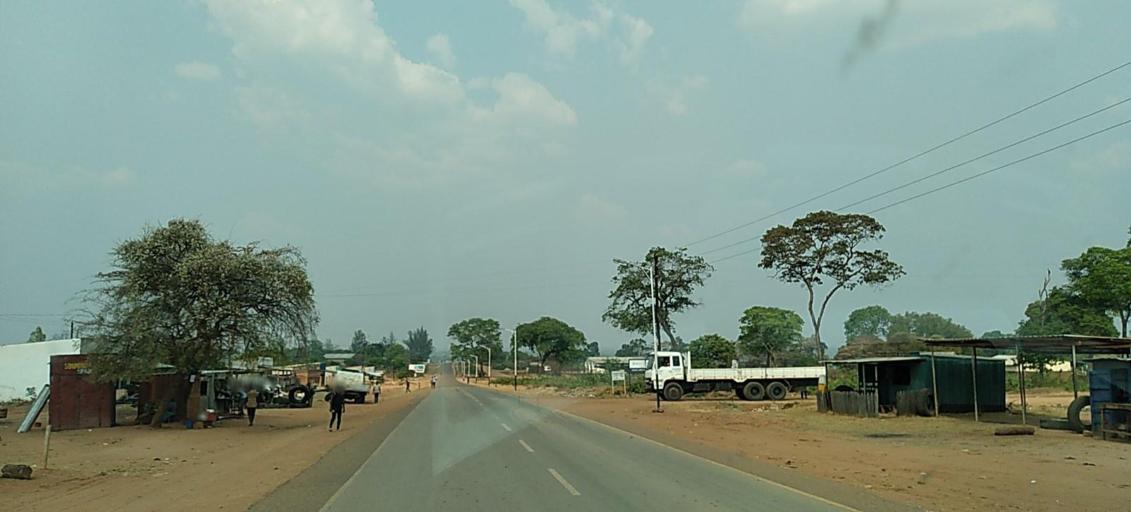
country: ZM
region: North-Western
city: Kabompo
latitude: -13.5935
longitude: 24.2022
